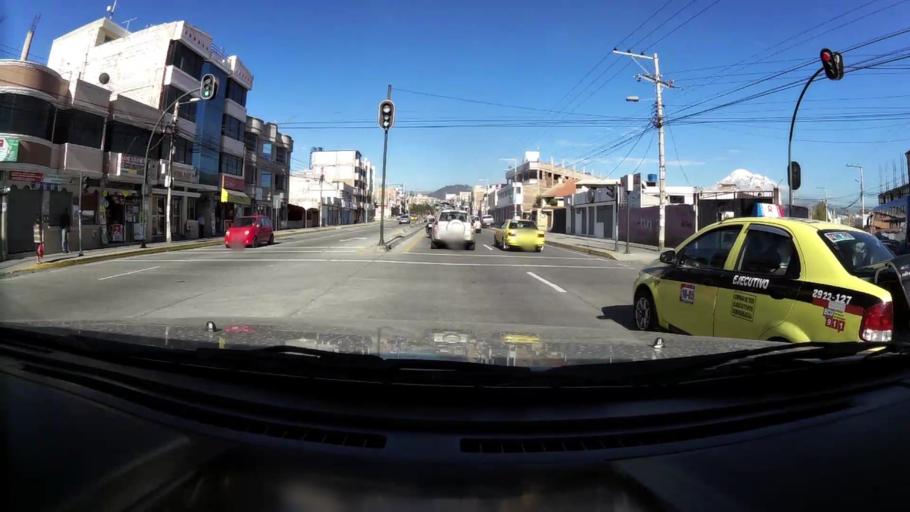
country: EC
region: Chimborazo
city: Riobamba
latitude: -1.6601
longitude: -78.6816
